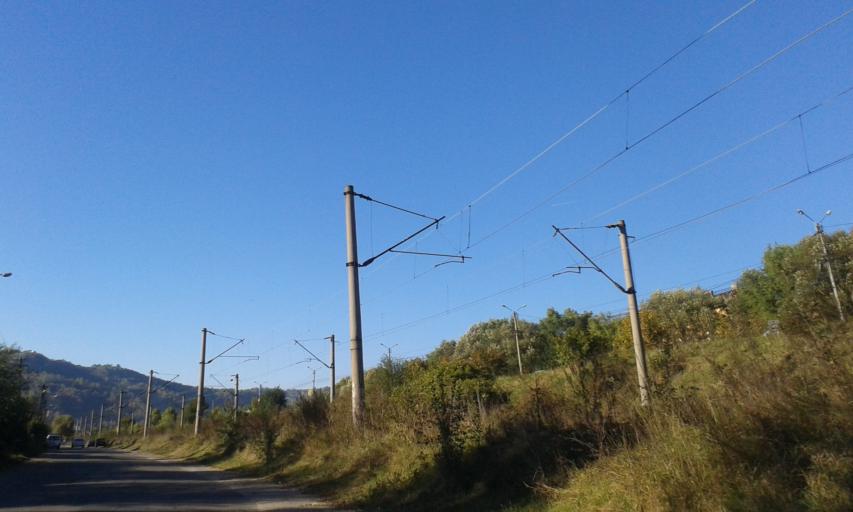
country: RO
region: Hunedoara
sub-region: Municipiul Petrosani
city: Petrosani
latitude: 45.4107
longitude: 23.3703
